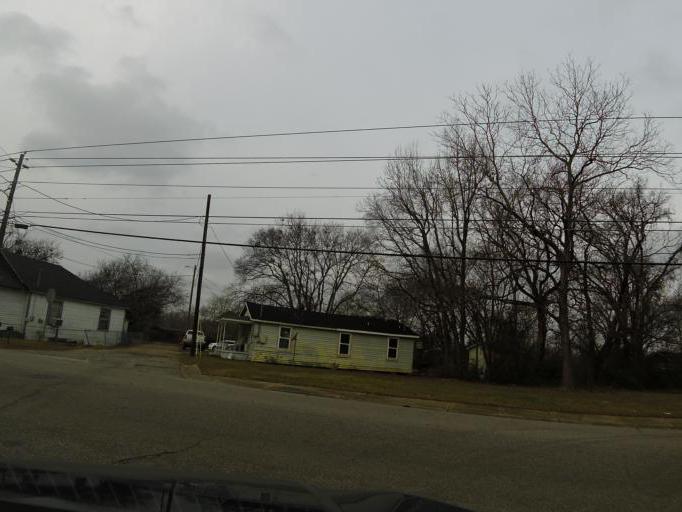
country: US
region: Alabama
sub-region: Montgomery County
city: Montgomery
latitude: 32.4092
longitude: -86.3032
